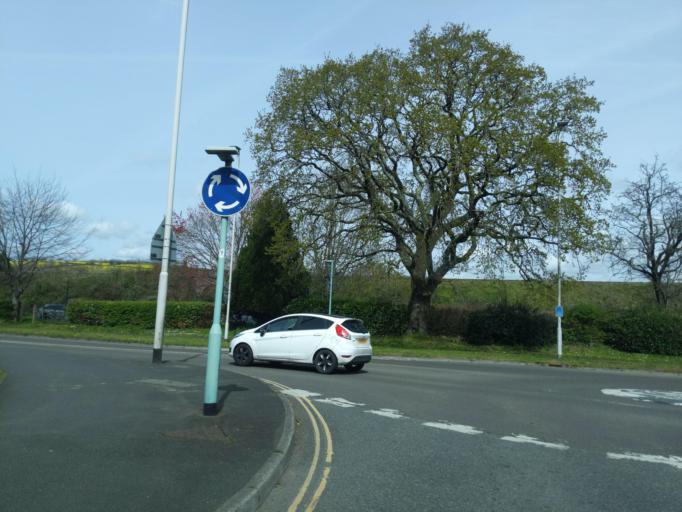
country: GB
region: England
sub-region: Devon
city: Plympton
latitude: 50.3918
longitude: -4.0495
